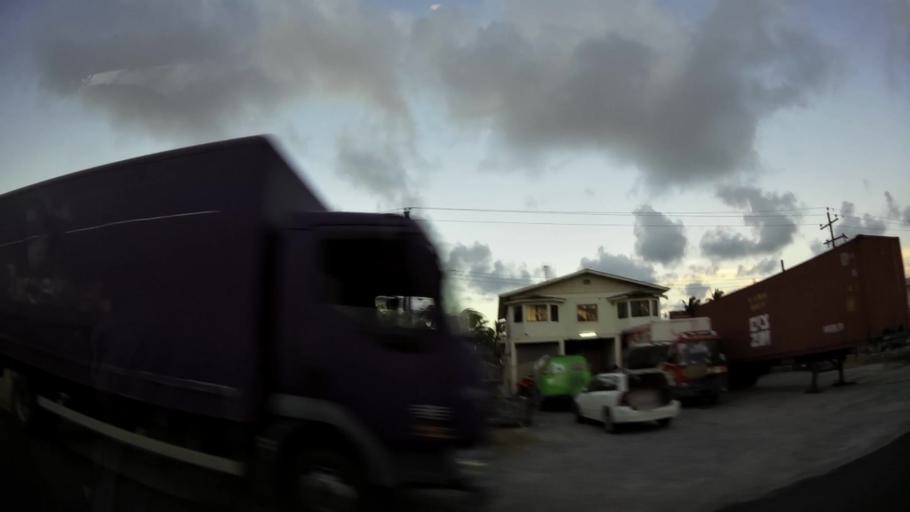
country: GY
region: Demerara-Mahaica
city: Georgetown
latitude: 6.8197
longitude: -58.0977
